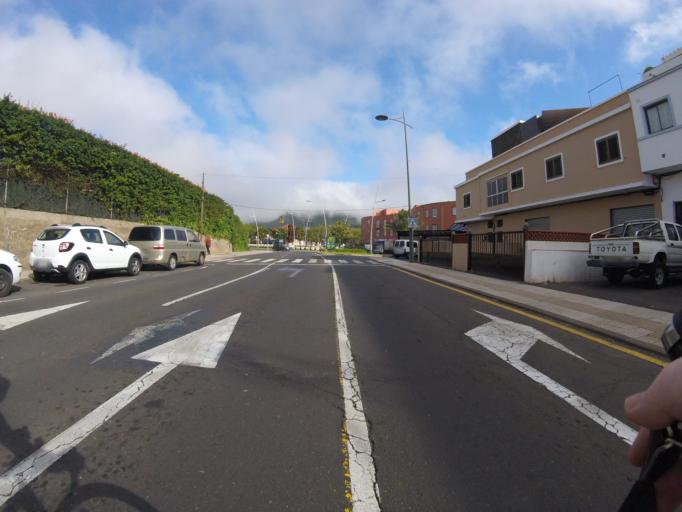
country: ES
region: Canary Islands
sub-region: Provincia de Santa Cruz de Tenerife
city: La Laguna
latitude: 28.4896
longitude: -16.3272
